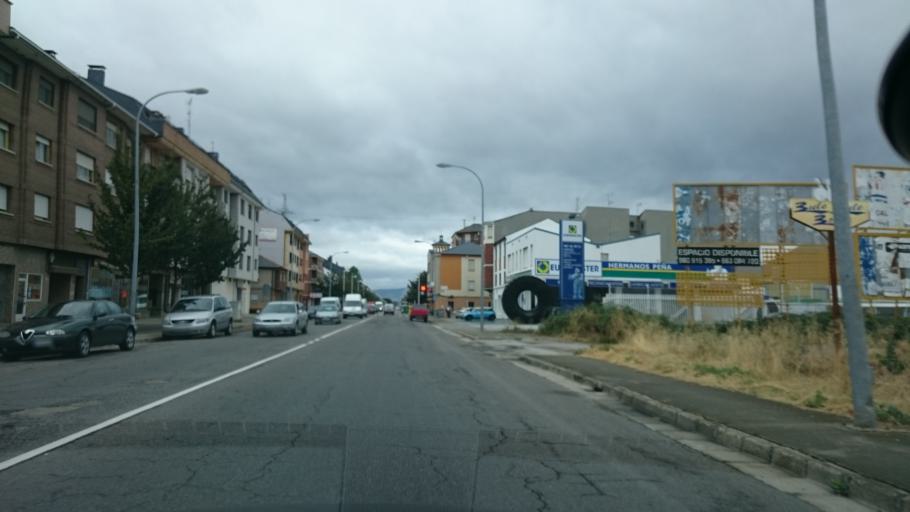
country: ES
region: Castille and Leon
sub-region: Provincia de Leon
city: Ponferrada
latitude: 42.5581
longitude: -6.6201
